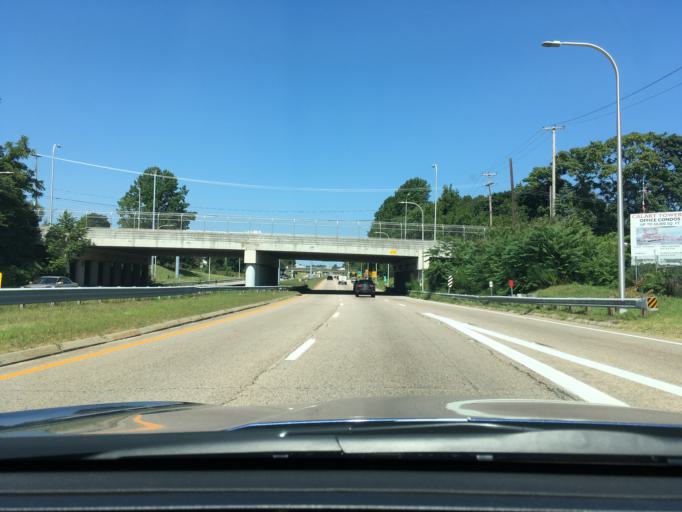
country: US
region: Rhode Island
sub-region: Providence County
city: Cranston
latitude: 41.7859
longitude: -71.4329
